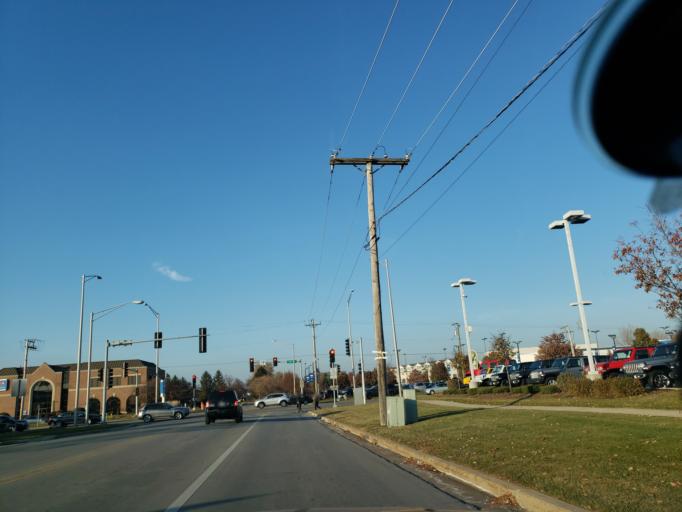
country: US
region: Illinois
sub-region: Cook County
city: Orland Hills
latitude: 41.6012
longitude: -87.8234
